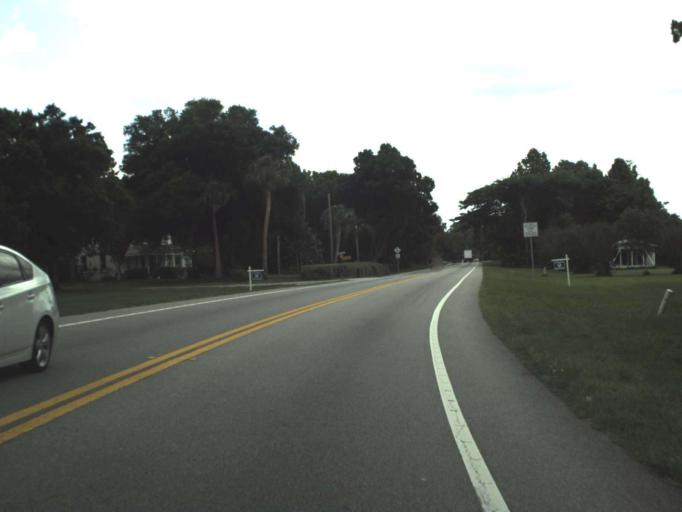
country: US
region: Florida
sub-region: Volusia County
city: Lake Helen
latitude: 29.0181
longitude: -81.2516
